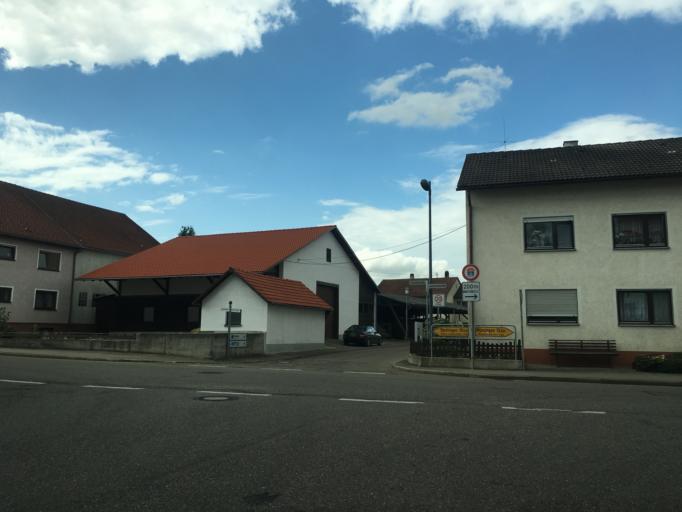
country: DE
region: Baden-Wuerttemberg
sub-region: Tuebingen Region
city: Gomadingen
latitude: 48.3512
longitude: 9.4276
